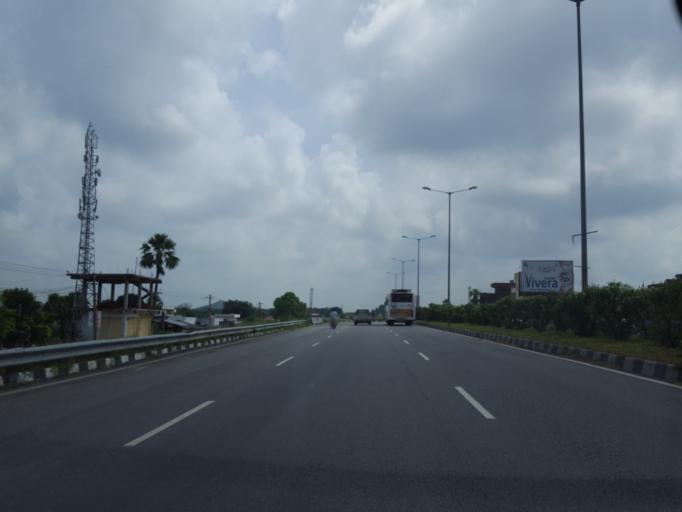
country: IN
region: Telangana
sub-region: Nalgonda
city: Nalgonda
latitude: 17.2293
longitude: 79.0205
